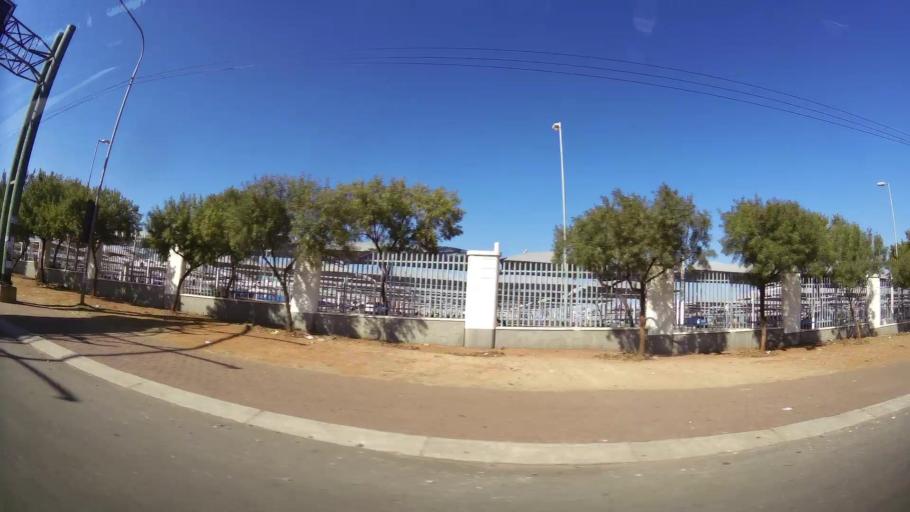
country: ZA
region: Gauteng
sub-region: City of Tshwane Metropolitan Municipality
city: Centurion
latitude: -25.8498
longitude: 28.1890
